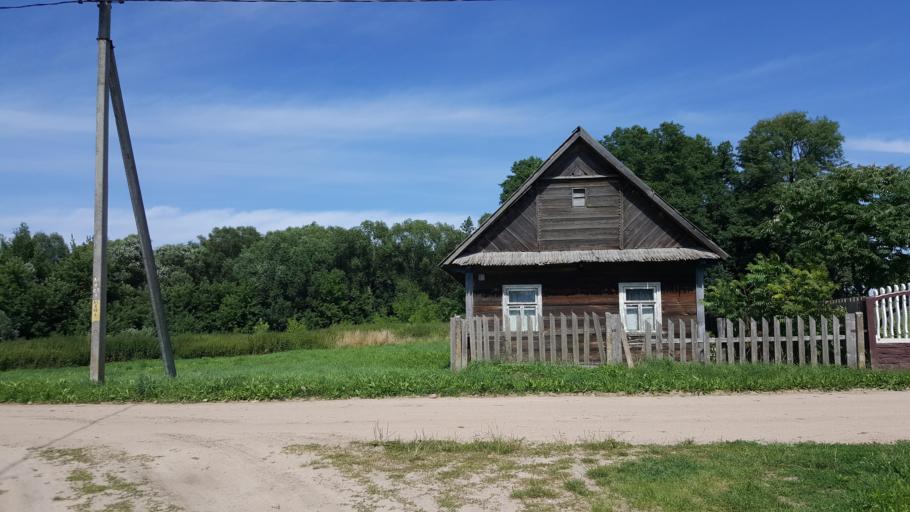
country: BY
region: Brest
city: Pruzhany
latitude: 52.5504
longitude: 24.2234
